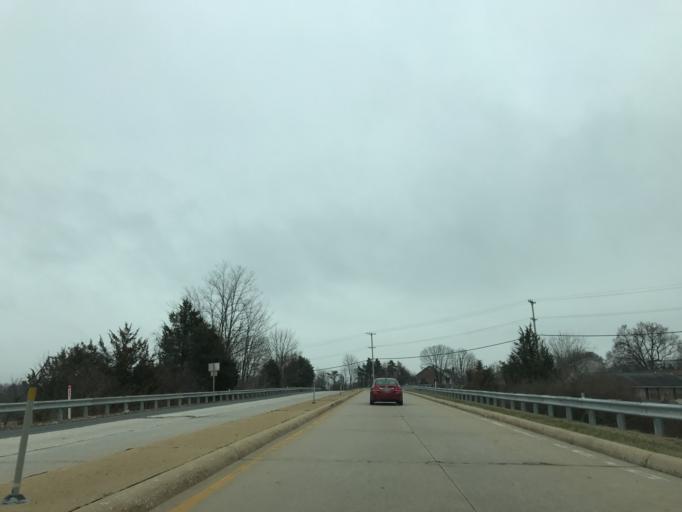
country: US
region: Maryland
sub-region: Carroll County
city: Westminster
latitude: 39.5922
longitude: -76.9981
